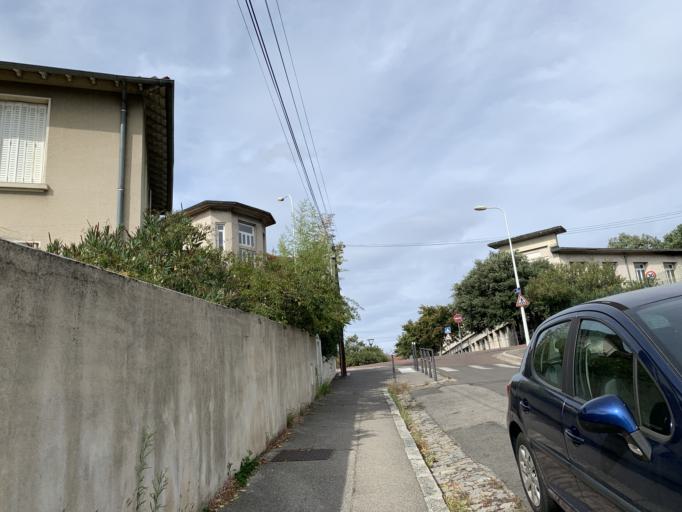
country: FR
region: Rhone-Alpes
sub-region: Departement du Rhone
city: Villeurbanne
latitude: 45.7477
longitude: 4.8920
